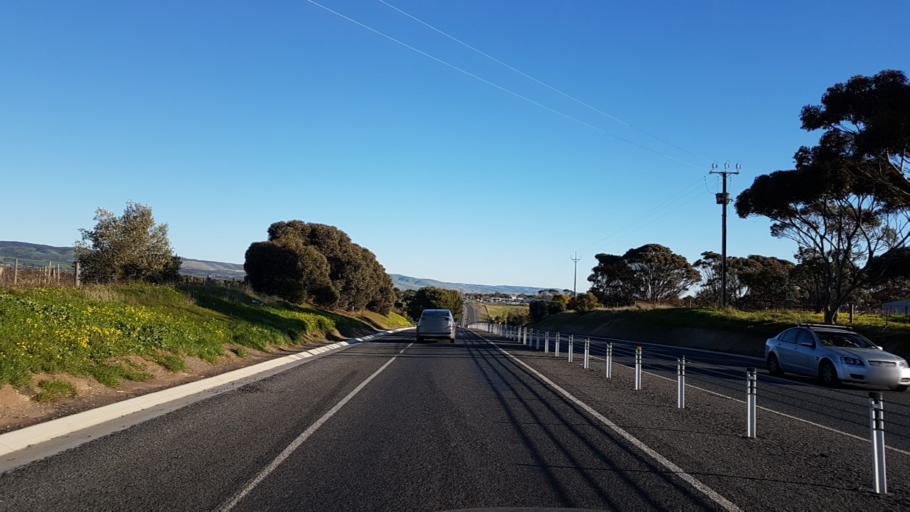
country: AU
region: South Australia
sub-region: Onkaparinga
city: Aldinga
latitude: -35.2607
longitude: 138.4900
